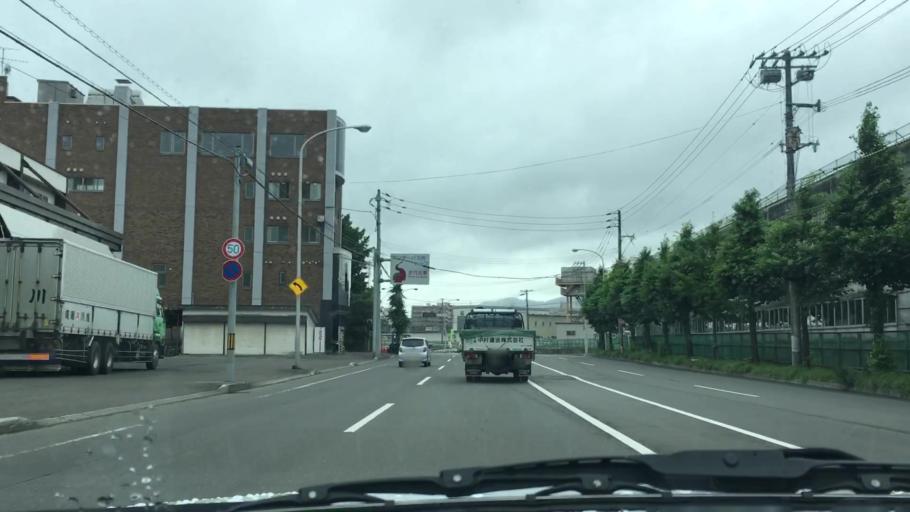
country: JP
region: Hokkaido
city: Sapporo
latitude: 43.0721
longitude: 141.3819
